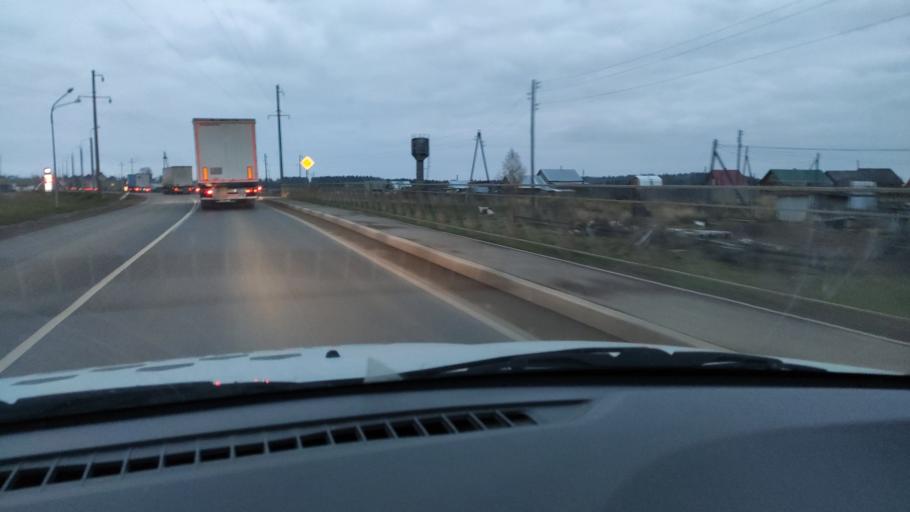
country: RU
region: Kirov
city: Kostino
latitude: 58.8516
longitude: 53.2665
